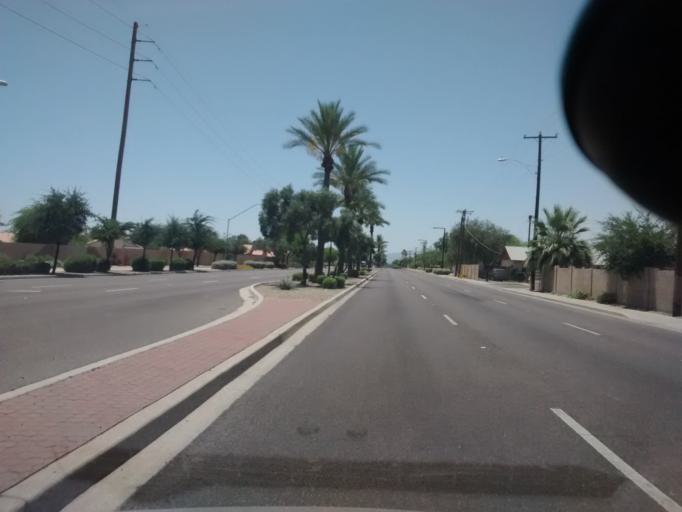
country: US
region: Arizona
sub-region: Maricopa County
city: Glendale
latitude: 33.5380
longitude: -112.2235
